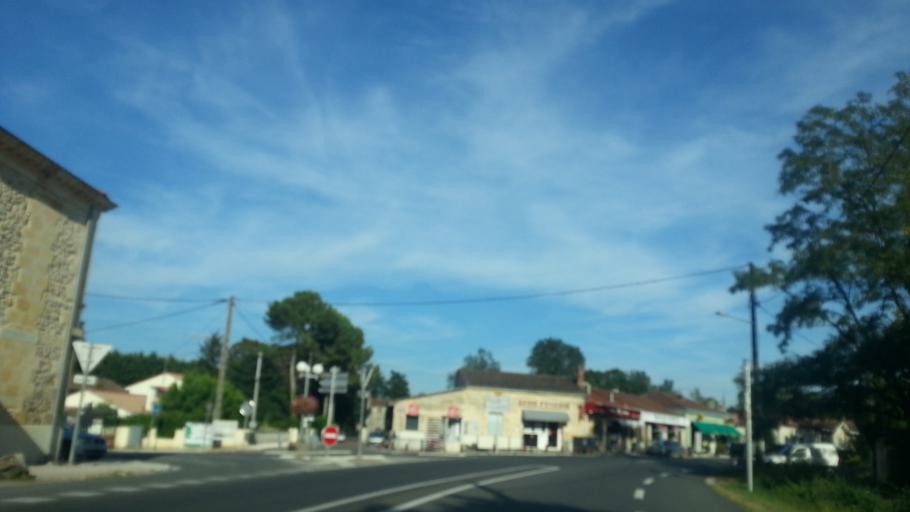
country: FR
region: Aquitaine
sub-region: Departement de la Gironde
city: Beautiran
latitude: 44.7000
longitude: -0.4502
